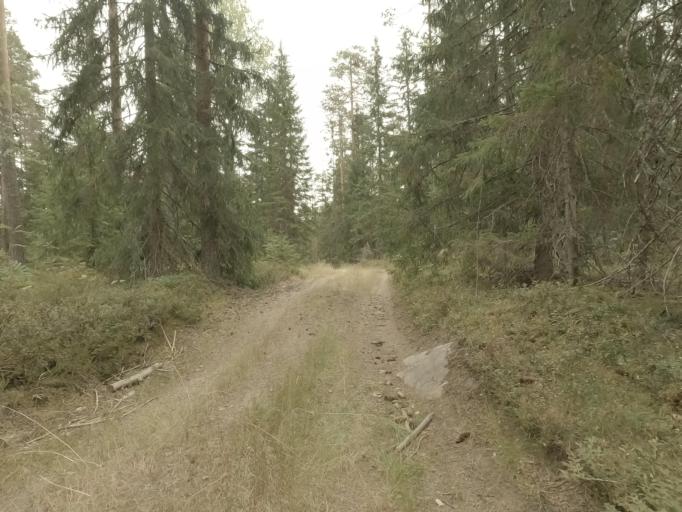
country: RU
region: Leningrad
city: Kamennogorsk
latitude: 61.0524
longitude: 29.1776
